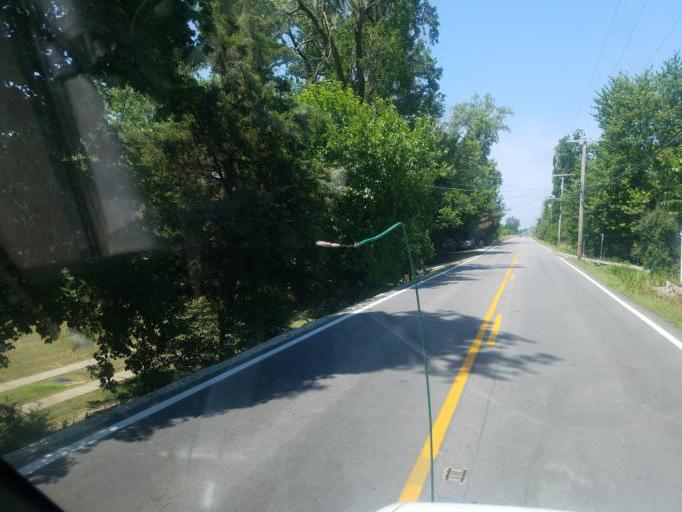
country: US
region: Ohio
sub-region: Auglaize County
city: Saint Marys
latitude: 40.5160
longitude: -84.4238
